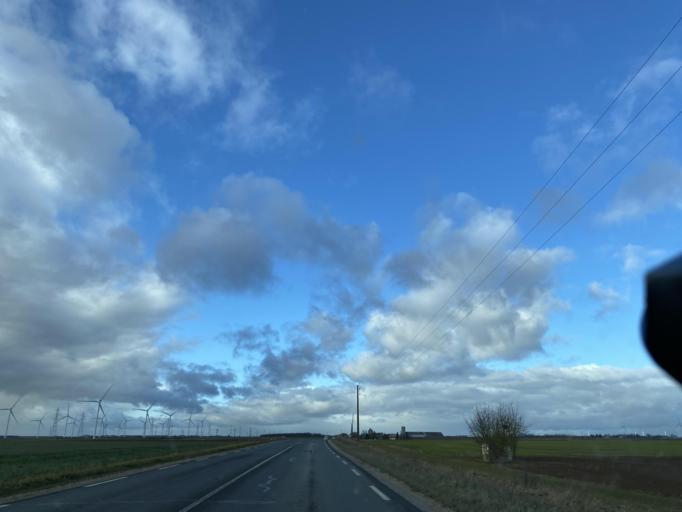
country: FR
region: Centre
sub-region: Departement d'Eure-et-Loir
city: Voves
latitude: 48.3085
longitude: 1.6868
